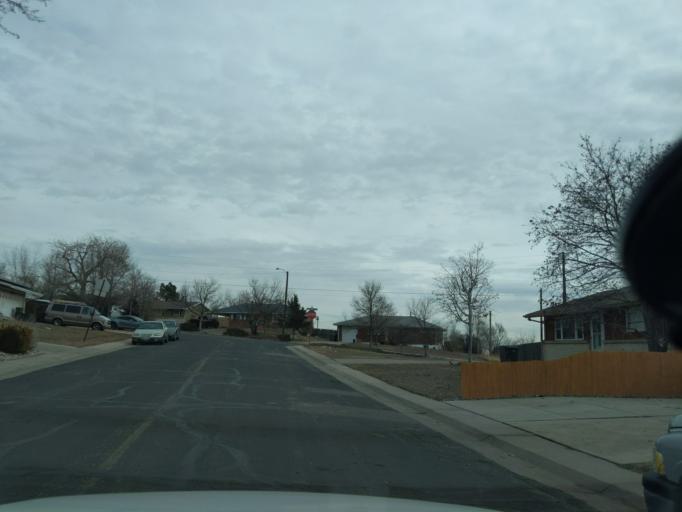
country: US
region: Colorado
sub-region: Adams County
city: Thornton
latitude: 39.8600
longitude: -104.9541
